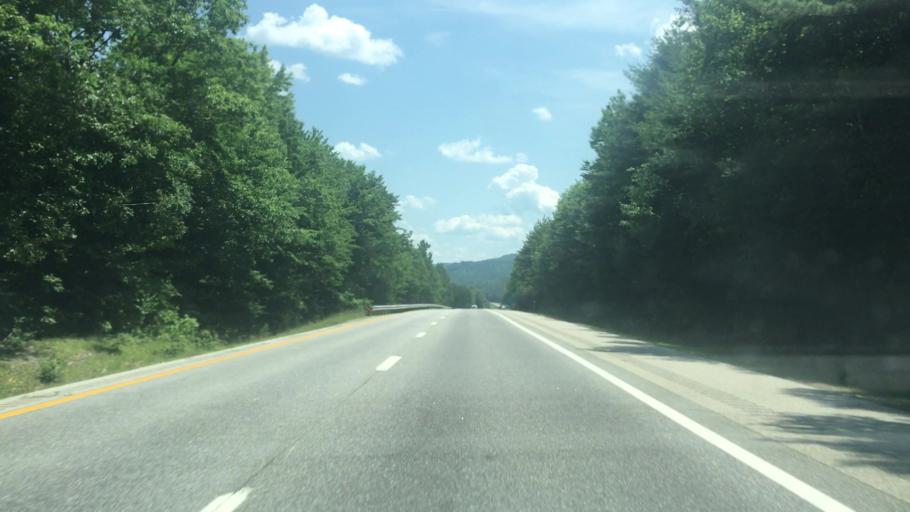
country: US
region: New Hampshire
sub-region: Merrimack County
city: Sutton
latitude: 43.3014
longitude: -71.8416
